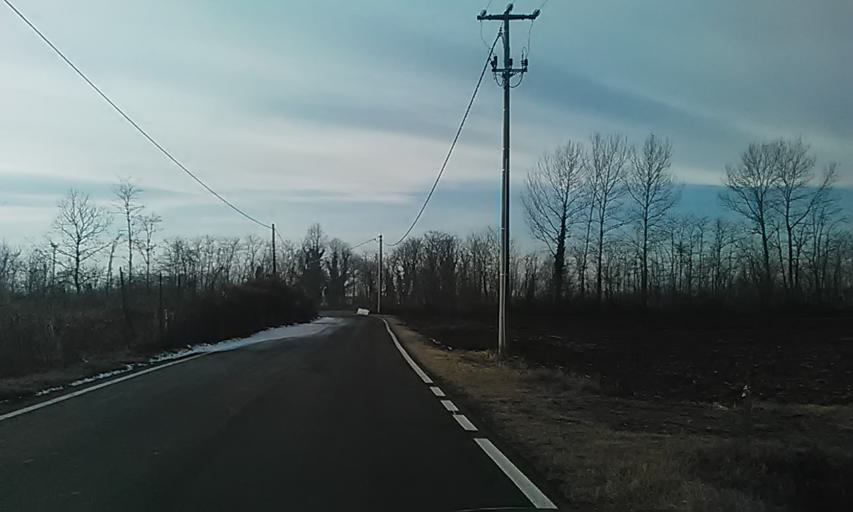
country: IT
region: Piedmont
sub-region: Provincia di Novara
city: Recetto
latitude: 45.4663
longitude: 8.4249
